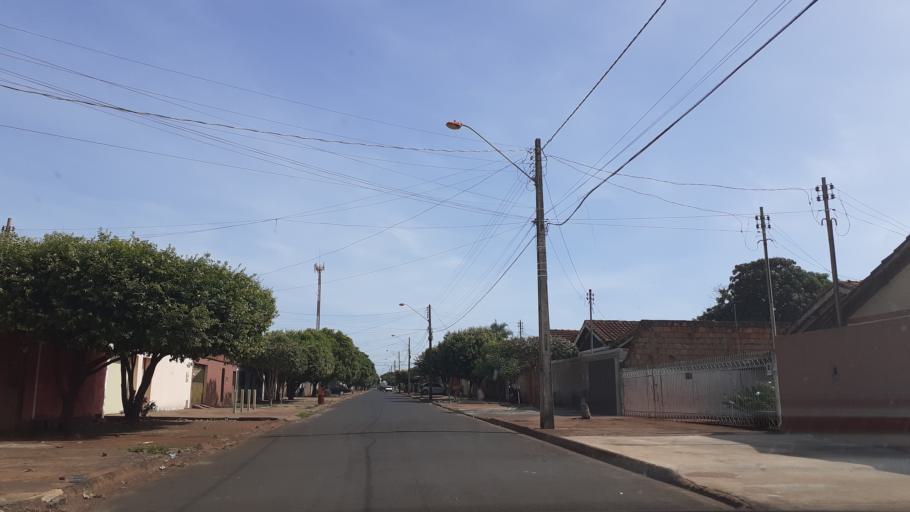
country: BR
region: Goias
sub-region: Itumbiara
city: Itumbiara
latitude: -18.4142
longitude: -49.2336
